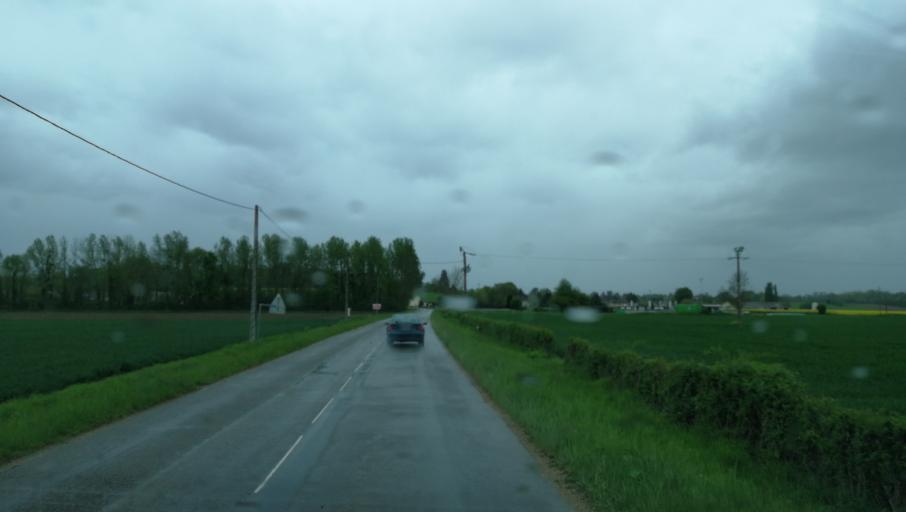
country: FR
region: Bourgogne
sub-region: Departement de Saone-et-Loire
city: Pierre-de-Bresse
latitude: 46.8958
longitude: 5.2596
